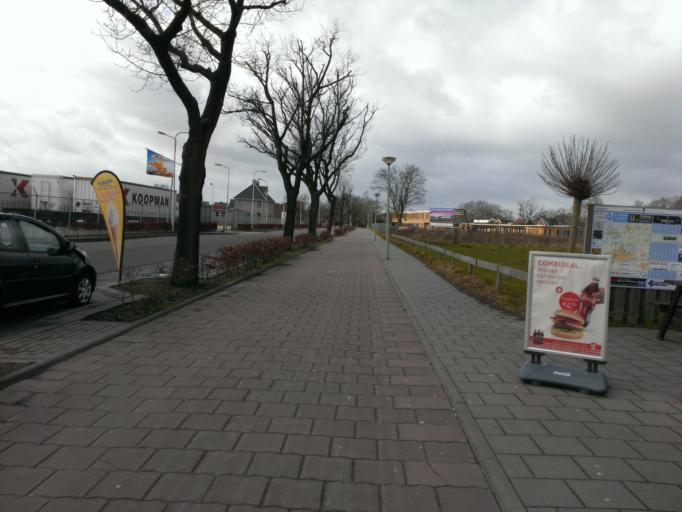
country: NL
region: Drenthe
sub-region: Gemeente Hoogeveen
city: Hoogeveen
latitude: 52.7347
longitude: 6.4817
